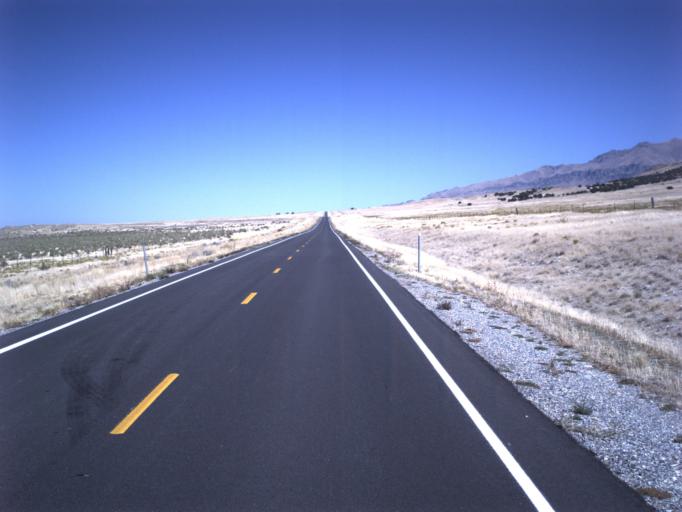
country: US
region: Utah
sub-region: Tooele County
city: Grantsville
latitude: 40.5590
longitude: -112.7363
